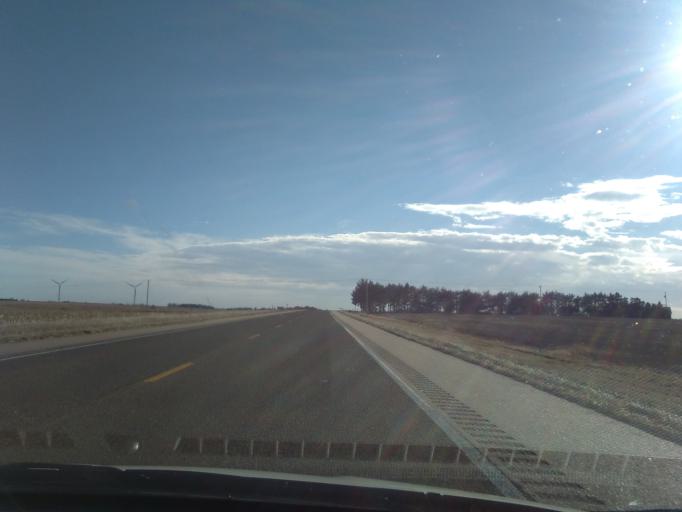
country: US
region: Nebraska
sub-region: Webster County
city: Red Cloud
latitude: 40.3087
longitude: -98.4438
